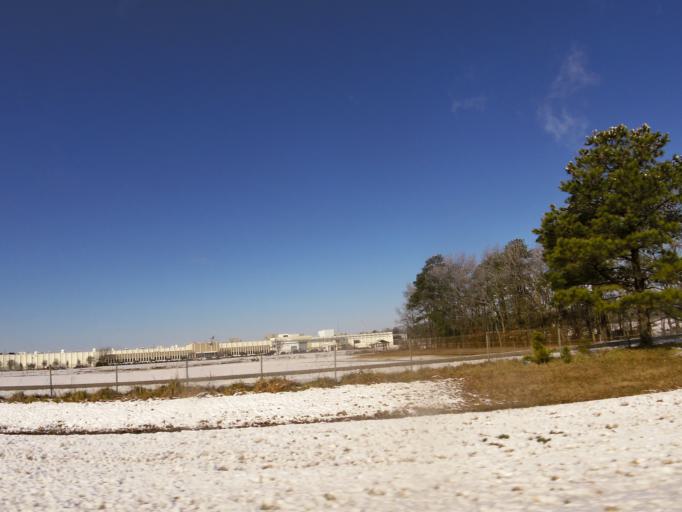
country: US
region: North Carolina
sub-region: Wilson County
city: Elm City
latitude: 35.7595
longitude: -77.8606
